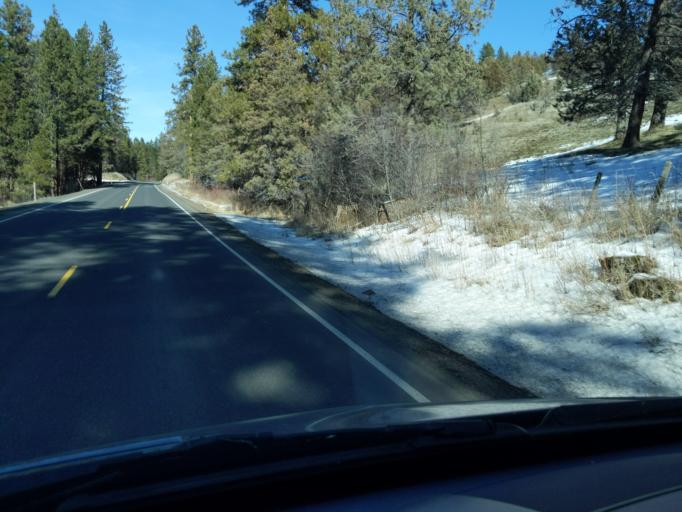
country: US
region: Oregon
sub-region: Grant County
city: John Day
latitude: 44.8688
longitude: -119.0229
